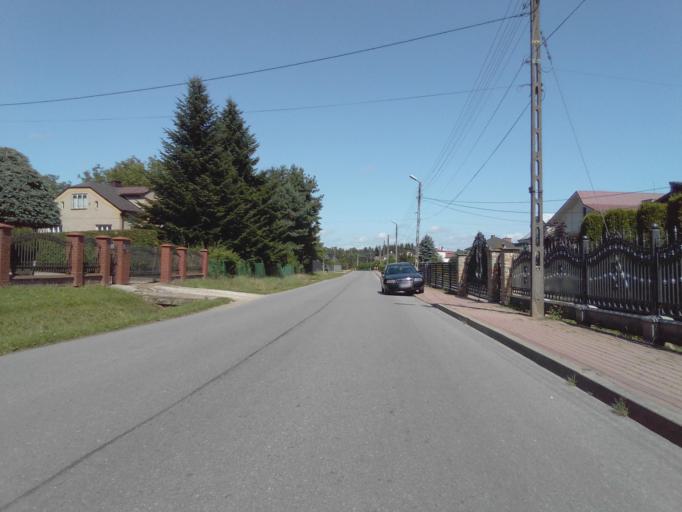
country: PL
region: Subcarpathian Voivodeship
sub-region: Powiat krosnienski
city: Jedlicze
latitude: 49.7176
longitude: 21.6371
